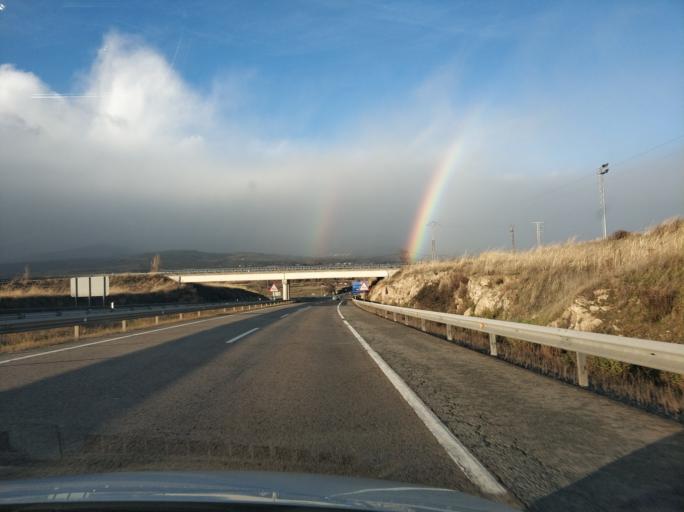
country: ES
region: Madrid
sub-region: Provincia de Madrid
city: Buitrago del Lozoya
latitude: 40.9905
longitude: -3.6420
